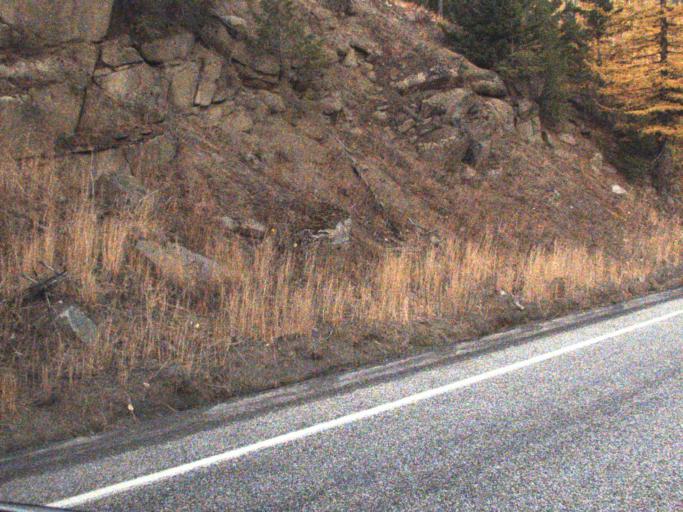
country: US
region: Washington
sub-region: Ferry County
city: Republic
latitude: 48.5987
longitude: -118.5139
